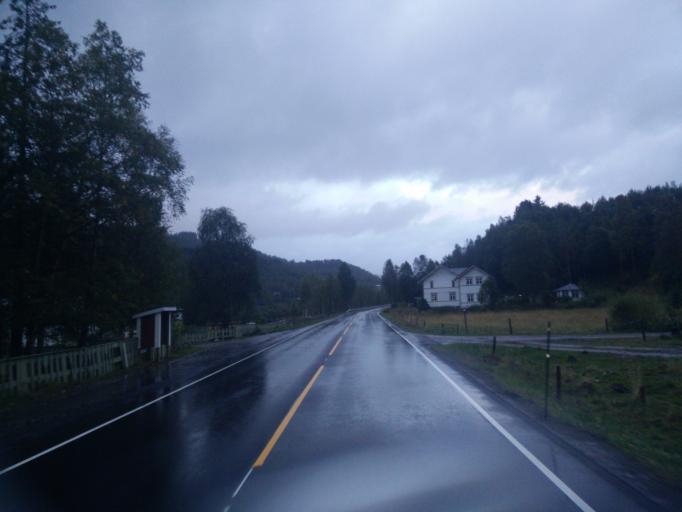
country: NO
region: More og Romsdal
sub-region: Rindal
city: Rindal
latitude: 63.0182
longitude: 9.0771
